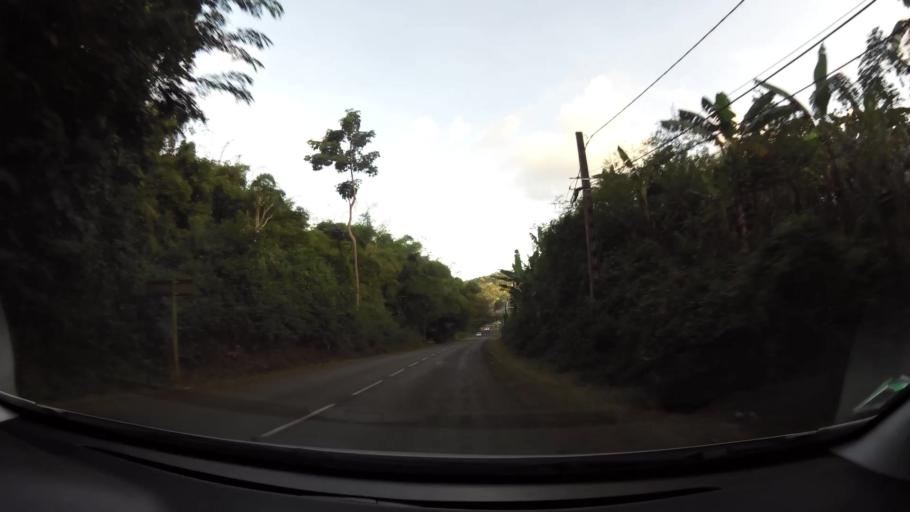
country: YT
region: Dembeni
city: Dembeni
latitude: -12.8636
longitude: 45.1981
